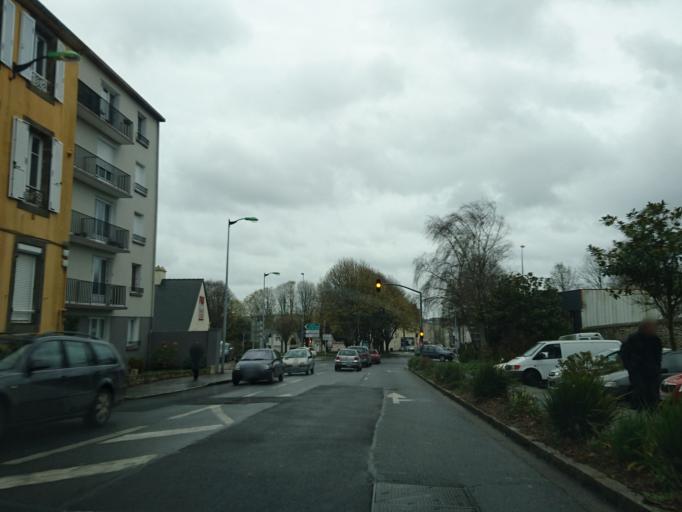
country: FR
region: Brittany
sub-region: Departement du Finistere
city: Brest
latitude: 48.4137
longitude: -4.4915
